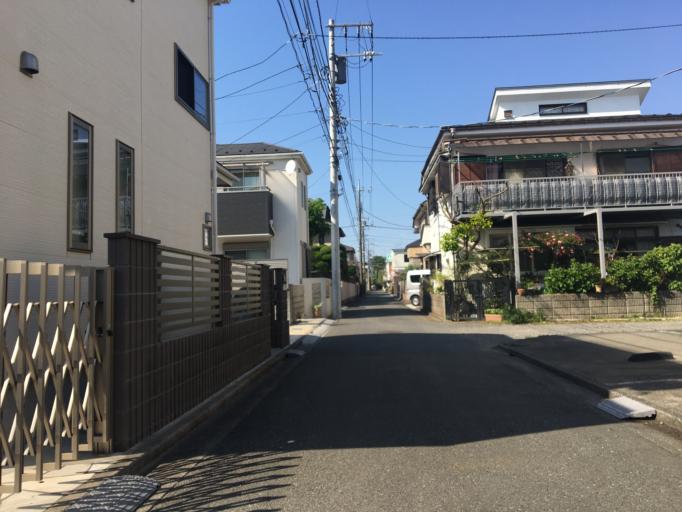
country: JP
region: Tokyo
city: Kokubunji
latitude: 35.7118
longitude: 139.4856
